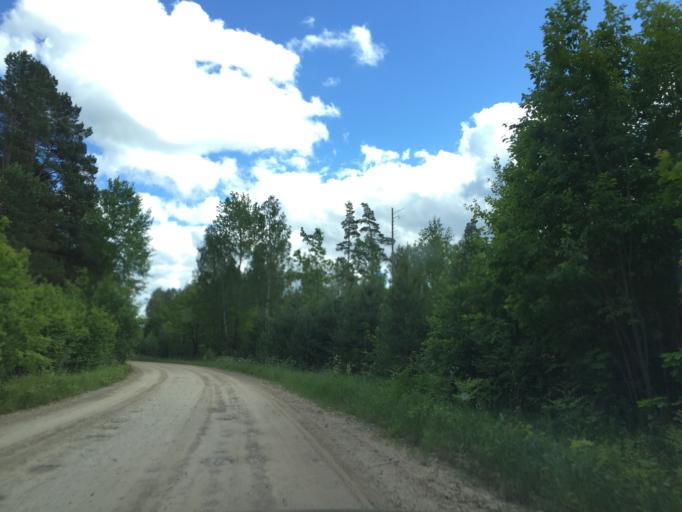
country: LV
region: Vecumnieki
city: Vecumnieki
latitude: 56.5048
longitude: 24.4000
